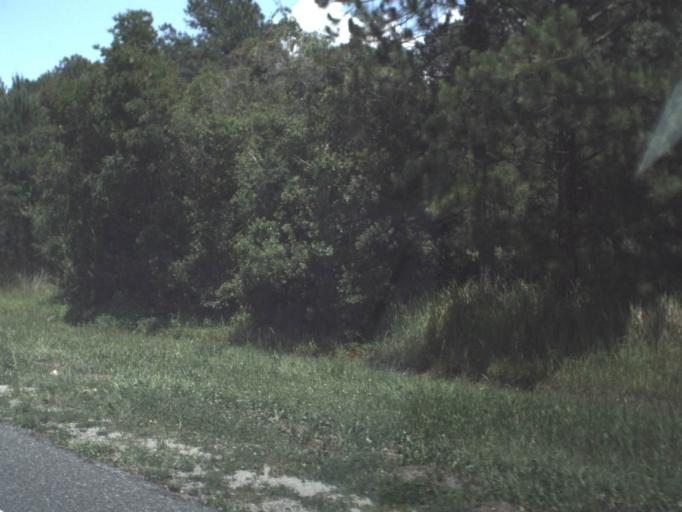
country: US
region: Florida
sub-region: Putnam County
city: Palatka
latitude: 29.7344
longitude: -81.6474
